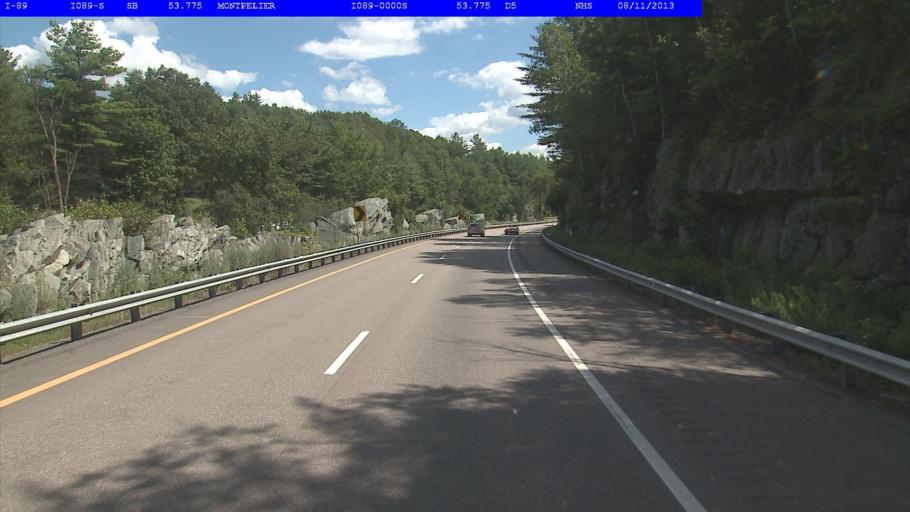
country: US
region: Vermont
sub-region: Washington County
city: Montpelier
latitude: 44.2604
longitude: -72.6043
